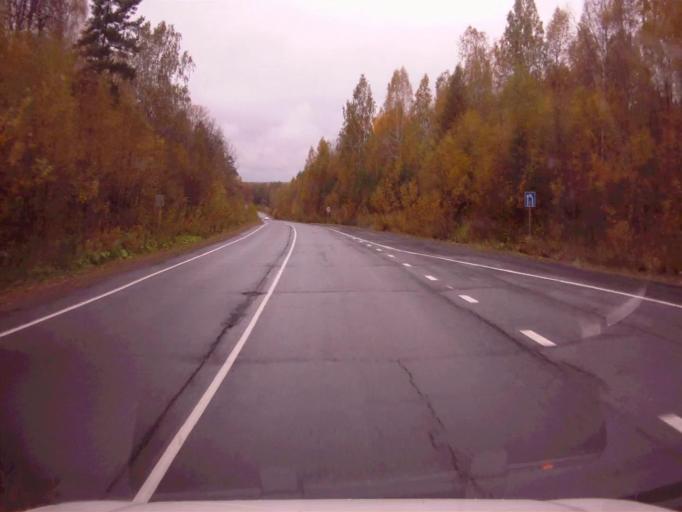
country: RU
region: Chelyabinsk
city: Nizhniy Ufaley
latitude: 56.0676
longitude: 60.0160
